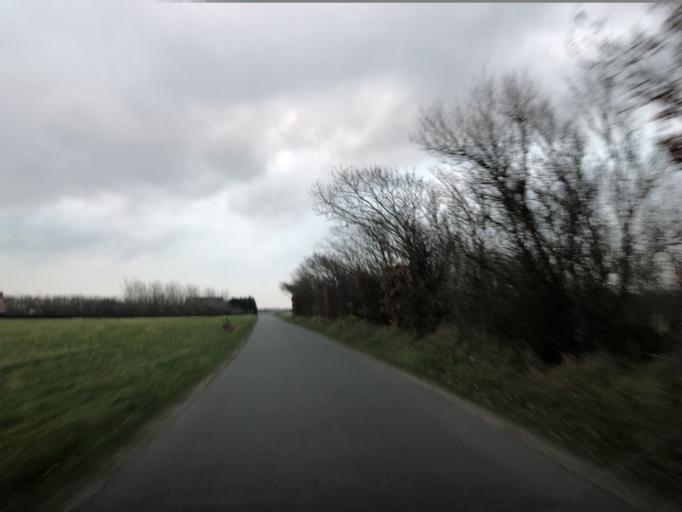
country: DK
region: Central Jutland
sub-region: Holstebro Kommune
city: Ulfborg
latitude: 56.2408
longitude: 8.2862
